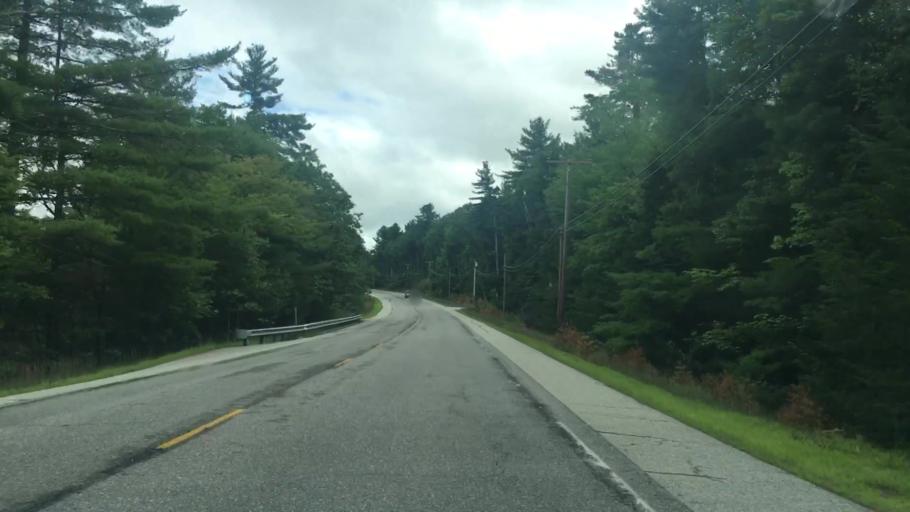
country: US
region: Maine
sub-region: York County
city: Lake Arrowhead
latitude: 43.6488
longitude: -70.7600
